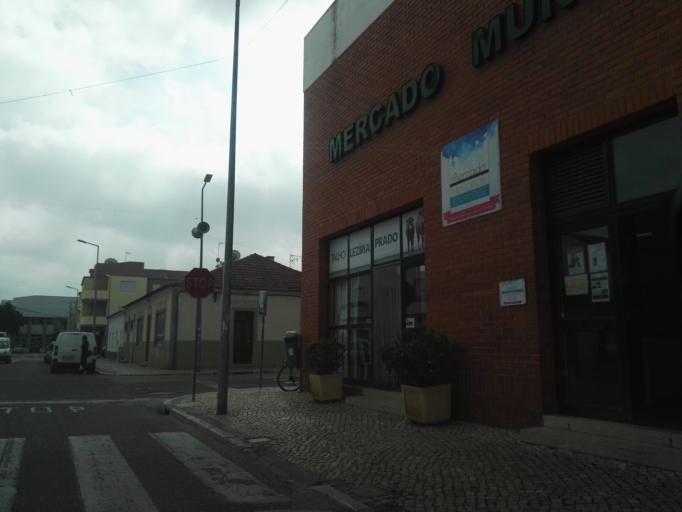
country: PT
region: Santarem
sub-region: Benavente
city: Benavente
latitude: 38.9793
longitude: -8.8076
